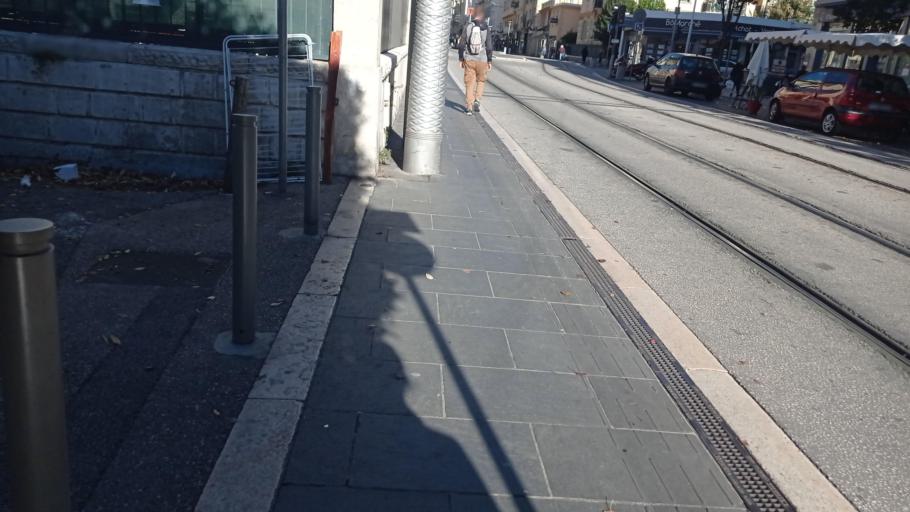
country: FR
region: Provence-Alpes-Cote d'Azur
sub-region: Departement des Alpes-Maritimes
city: Nice
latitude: 43.7110
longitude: 7.2619
